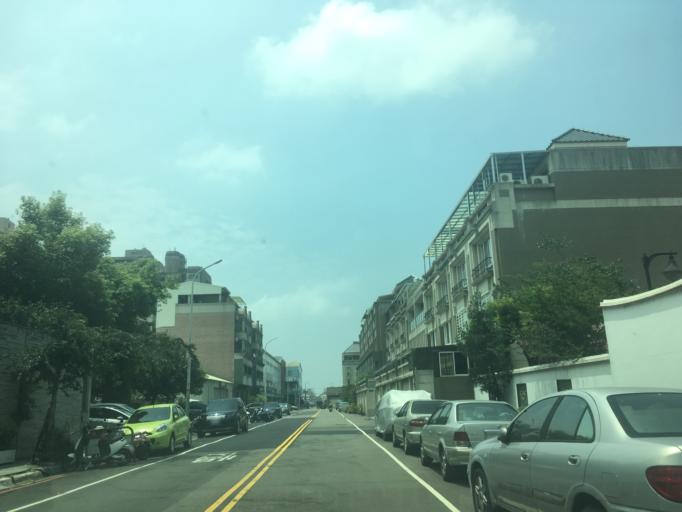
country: TW
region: Taiwan
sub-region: Taichung City
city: Taichung
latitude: 24.1767
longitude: 120.6837
